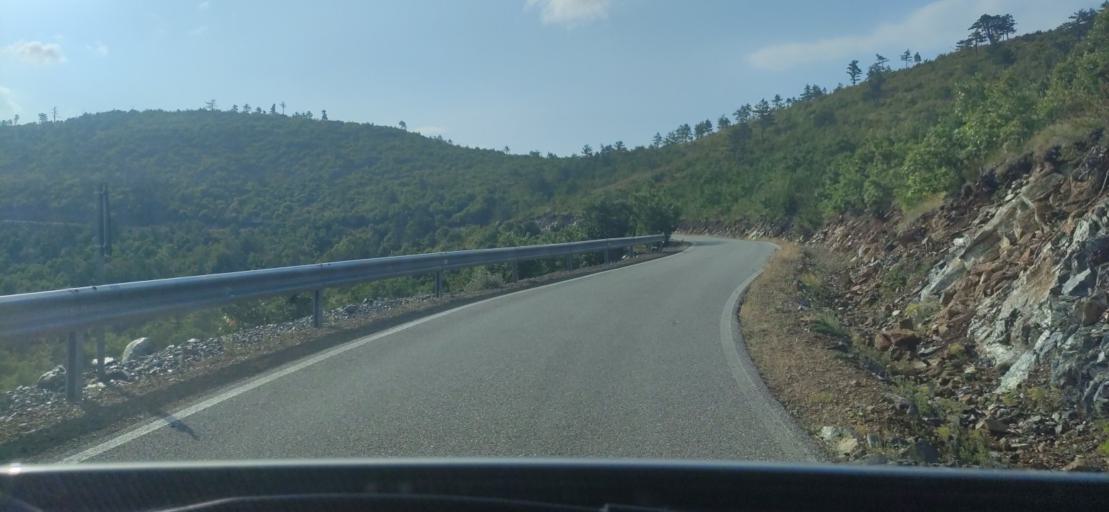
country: AL
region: Shkoder
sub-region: Rrethi i Pukes
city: Iballe
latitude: 42.1710
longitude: 20.0073
